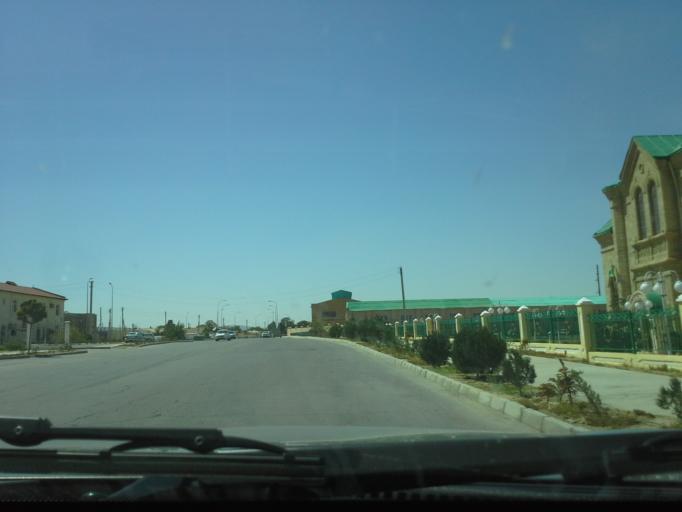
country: TM
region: Balkan
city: Serdar
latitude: 38.9773
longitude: 56.2767
